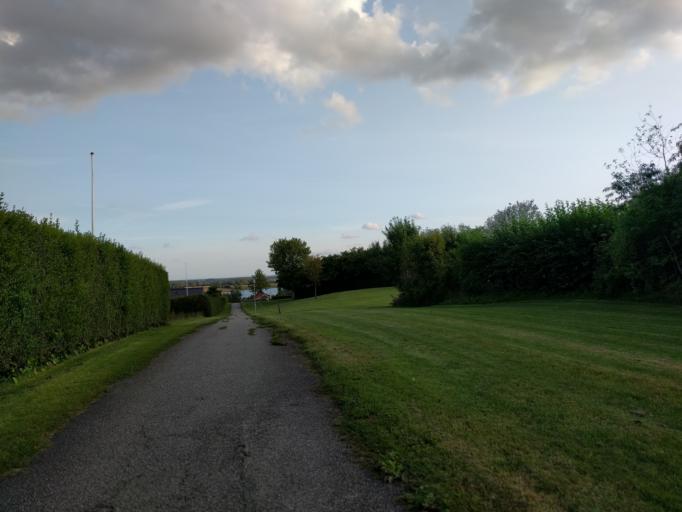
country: DK
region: South Denmark
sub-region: Kerteminde Kommune
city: Munkebo
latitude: 55.4668
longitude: 10.5806
